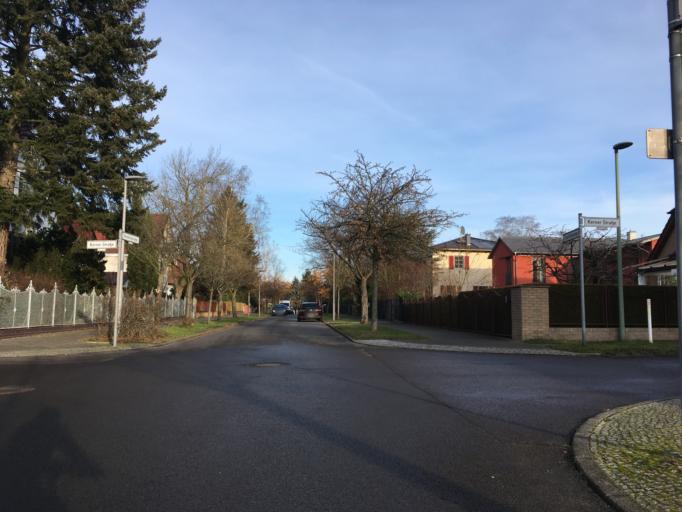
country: DE
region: Berlin
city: Blankenburg
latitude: 52.6110
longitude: 13.4609
